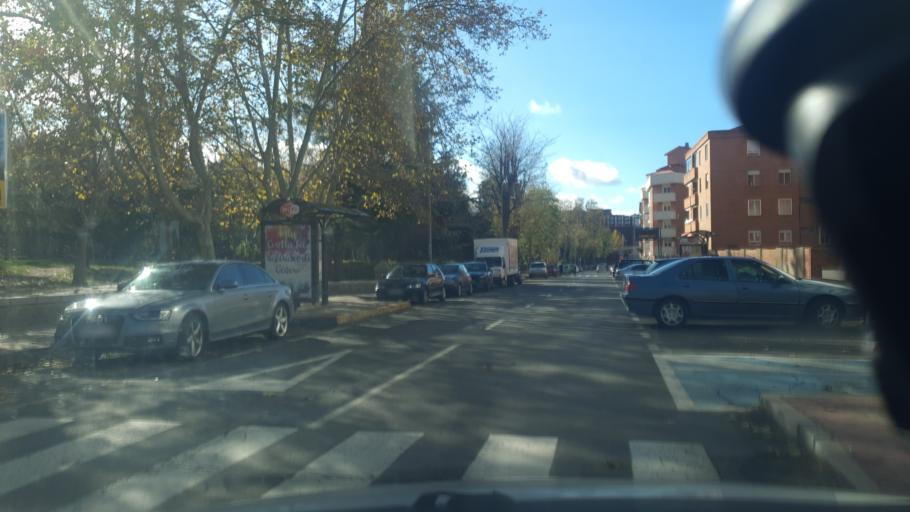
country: ES
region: Castille and Leon
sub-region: Provincia de Avila
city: Avila
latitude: 40.6595
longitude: -4.6858
